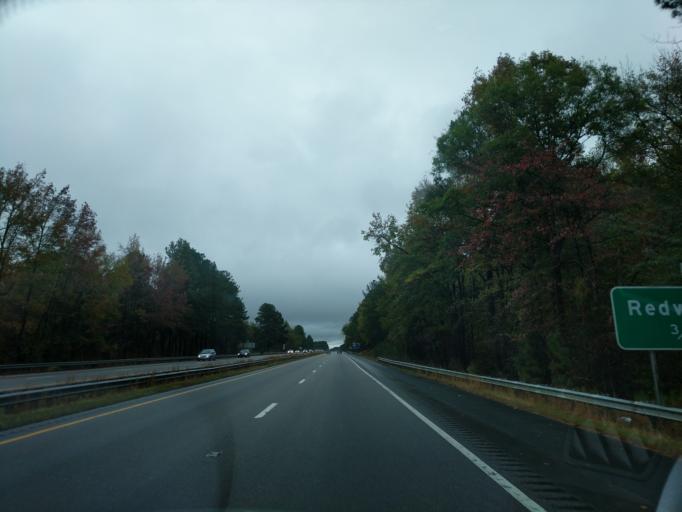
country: US
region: North Carolina
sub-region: Durham County
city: Gorman
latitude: 36.0522
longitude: -78.8046
